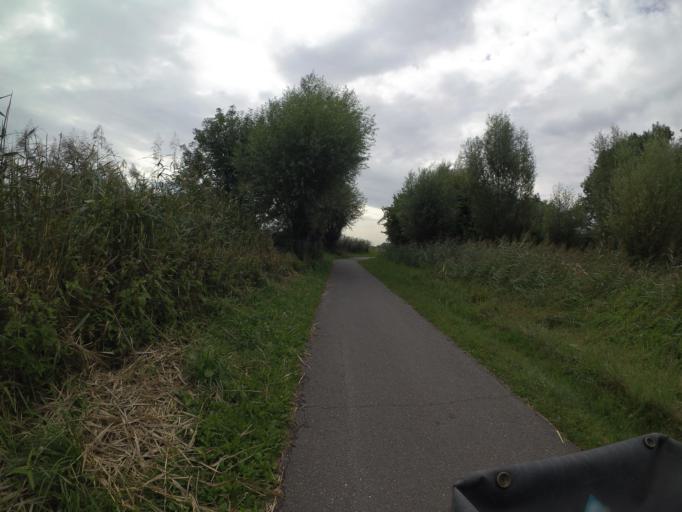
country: NL
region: North Brabant
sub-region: Roosendaal
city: Roosendaal
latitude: 51.5048
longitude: 4.4521
